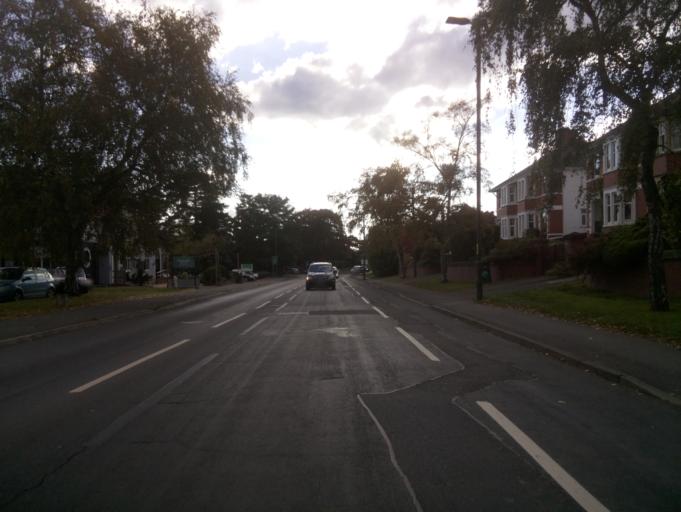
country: GB
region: England
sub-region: Herefordshire
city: Hereford
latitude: 52.0566
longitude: -2.6963
